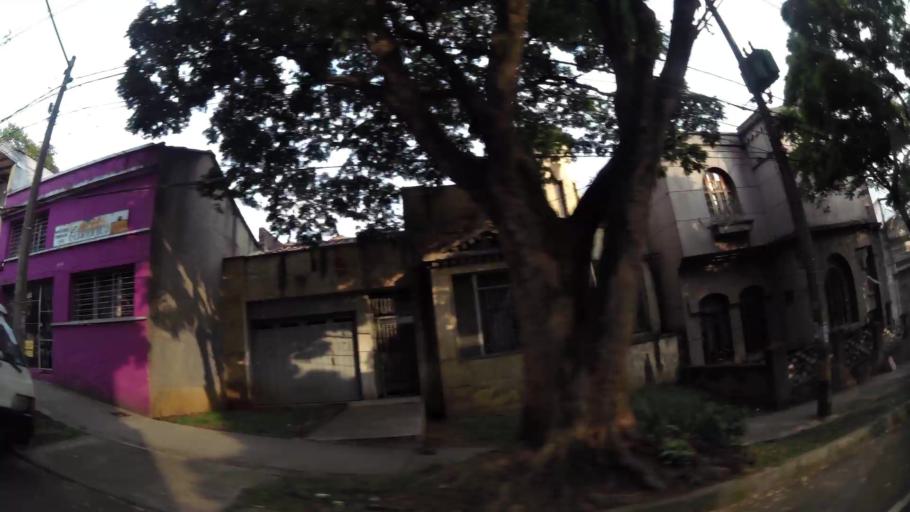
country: CO
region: Antioquia
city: Medellin
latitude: 6.2571
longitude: -75.5633
